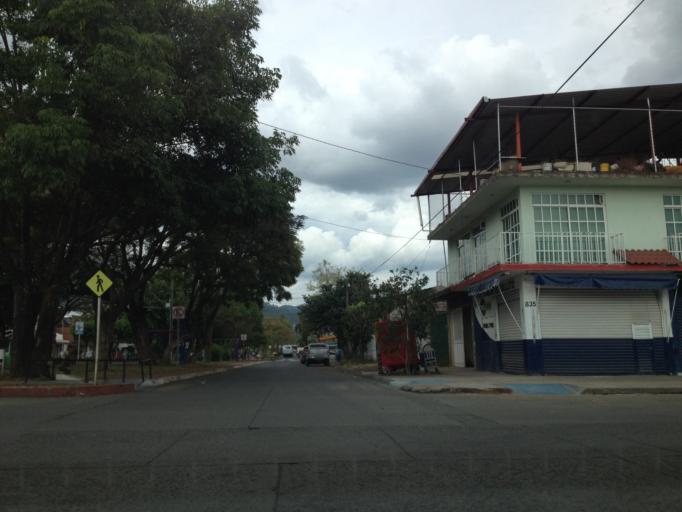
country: MX
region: Michoacan
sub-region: Uruapan
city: Uruapan
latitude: 19.4125
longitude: -102.0377
